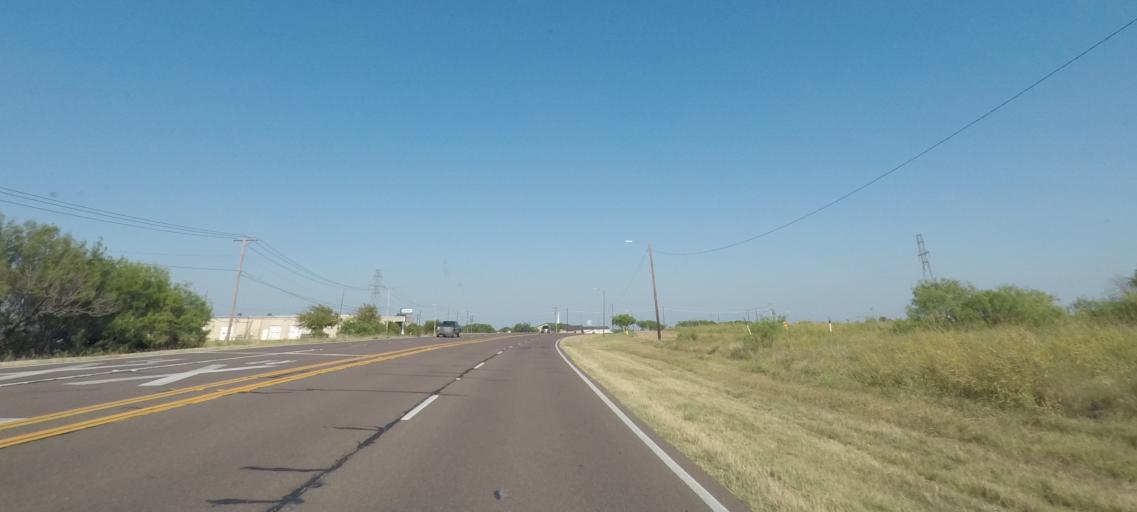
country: US
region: Texas
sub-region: Wichita County
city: Wichita Falls
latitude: 33.8593
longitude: -98.5901
